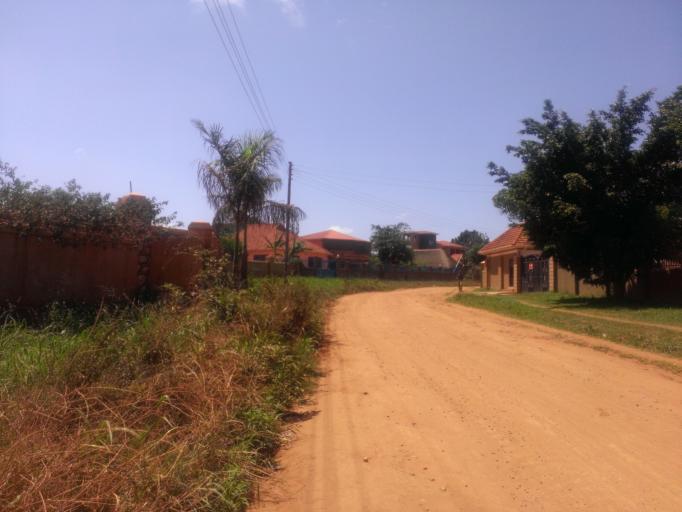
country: UG
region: Northern Region
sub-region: Gulu District
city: Gulu
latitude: 2.7871
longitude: 32.3021
